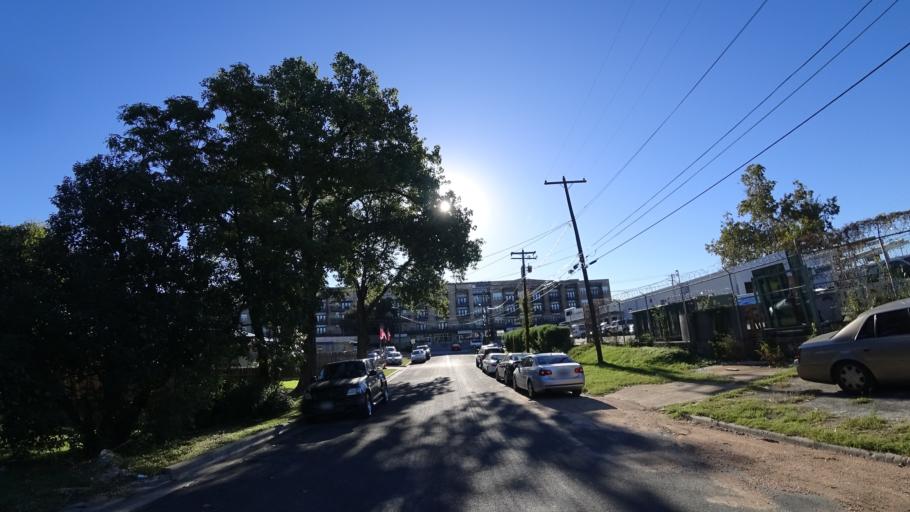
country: US
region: Texas
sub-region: Travis County
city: Austin
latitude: 30.2262
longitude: -97.7631
